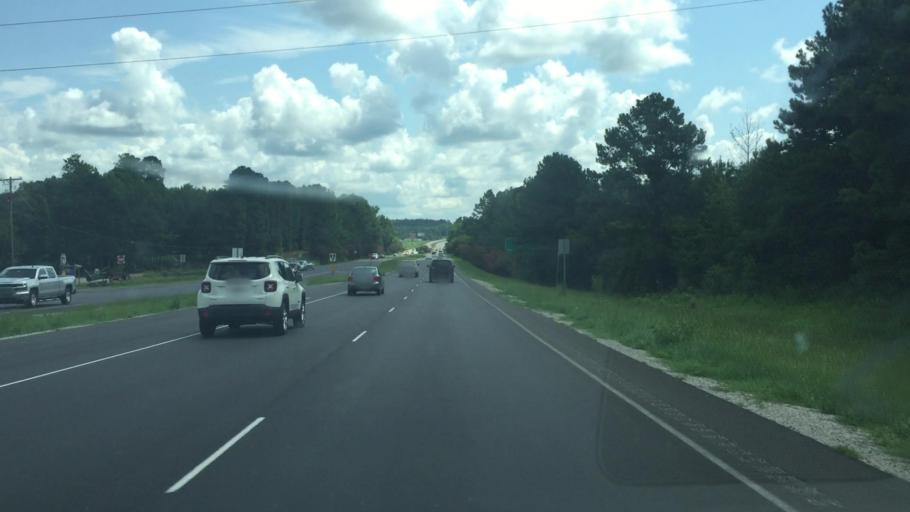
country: US
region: North Carolina
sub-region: Richmond County
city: Cordova
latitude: 34.9445
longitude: -79.8806
